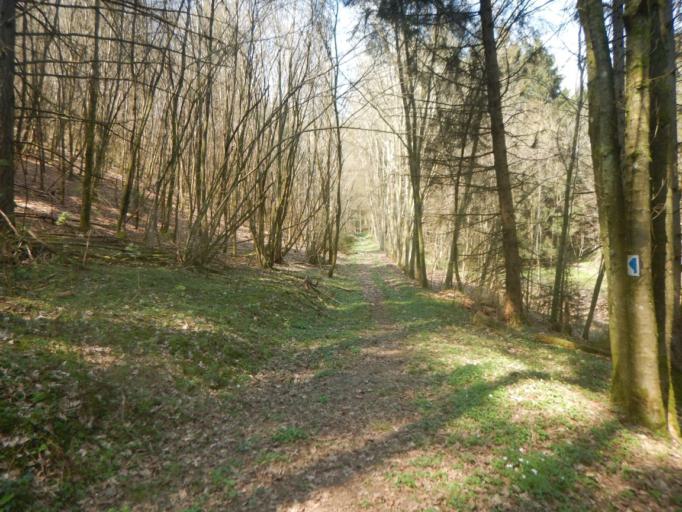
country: LU
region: Diekirch
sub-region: Canton de Clervaux
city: Clervaux
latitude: 50.0504
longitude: 6.0132
